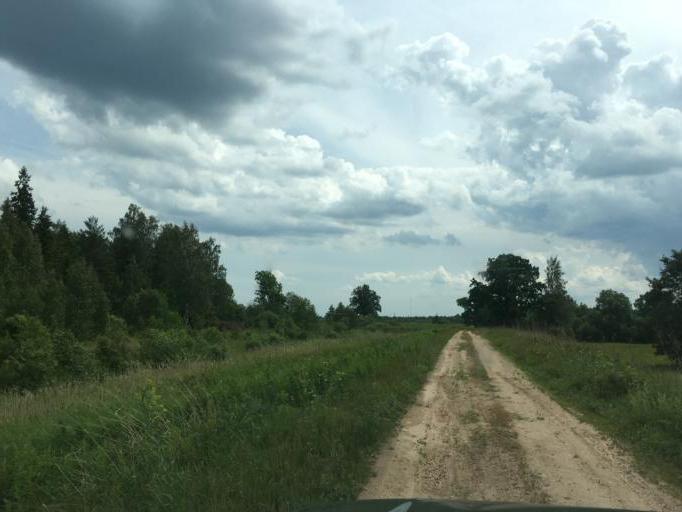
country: LV
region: Rugaju
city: Rugaji
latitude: 56.9775
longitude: 27.0505
